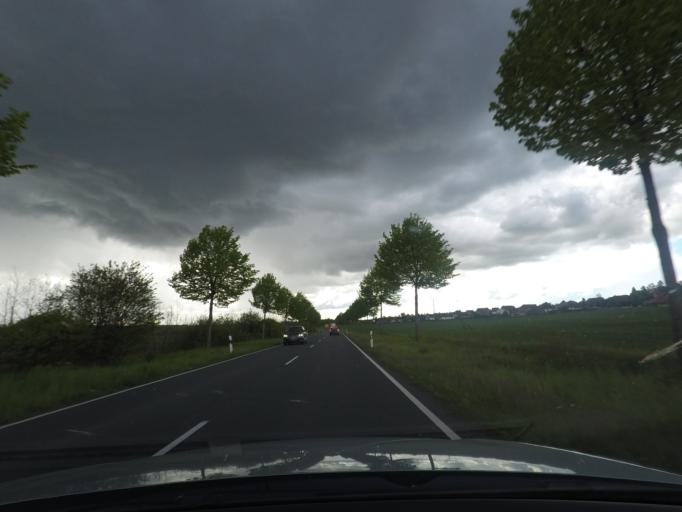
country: DE
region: Lower Saxony
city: Helmstedt
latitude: 52.2135
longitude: 11.0272
